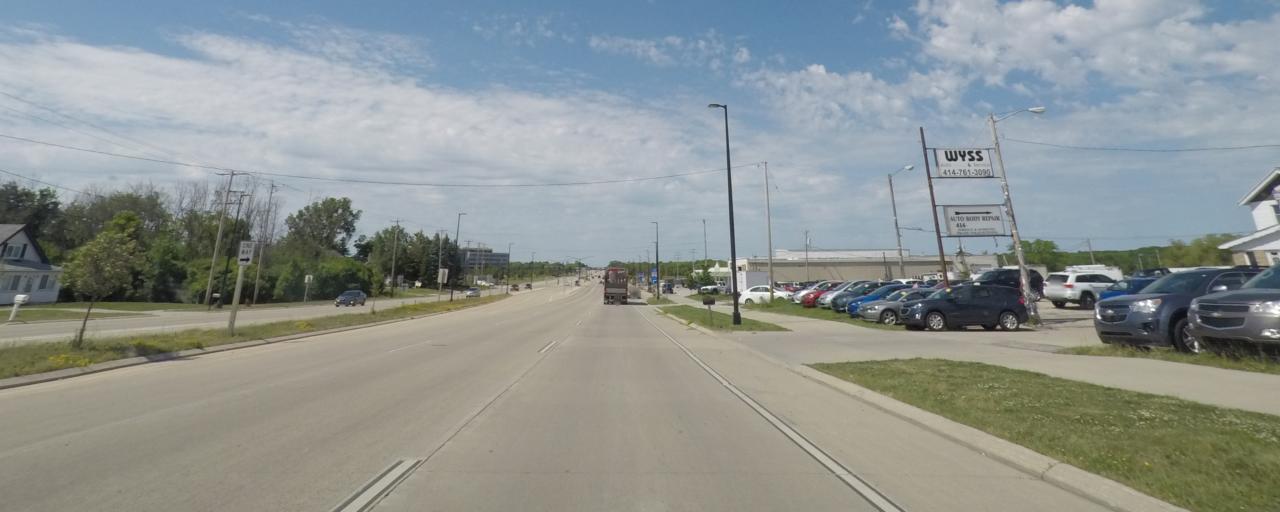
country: US
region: Wisconsin
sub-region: Milwaukee County
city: Greendale
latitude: 42.8994
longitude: -87.9503
